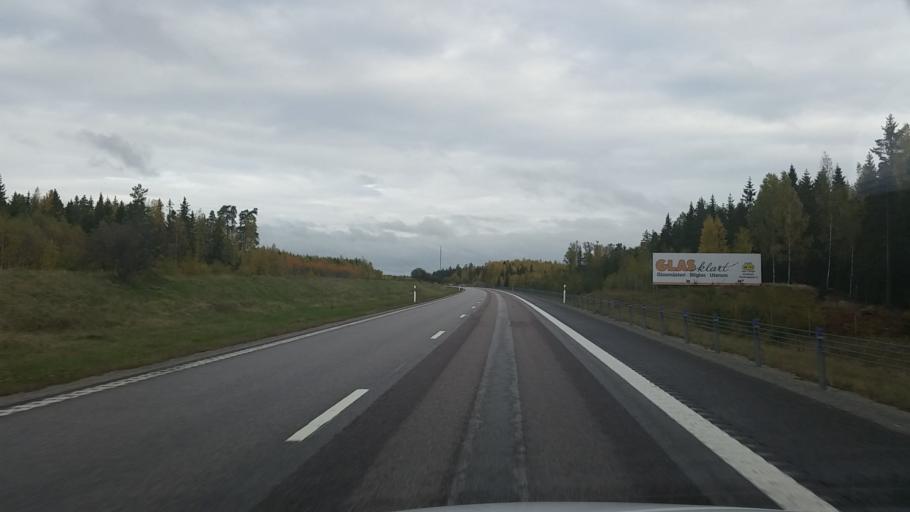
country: SE
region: Uppsala
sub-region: Osthammars Kommun
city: Bjorklinge
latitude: 60.0331
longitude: 17.6297
